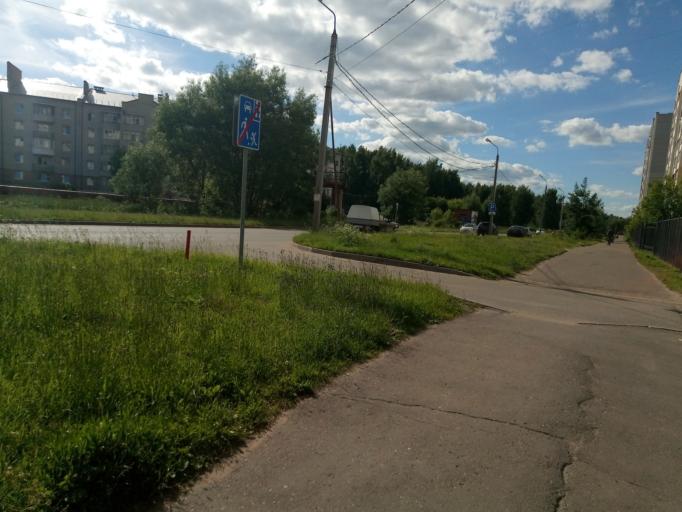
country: RU
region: Jaroslavl
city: Yaroslavl
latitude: 57.6395
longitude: 39.9483
